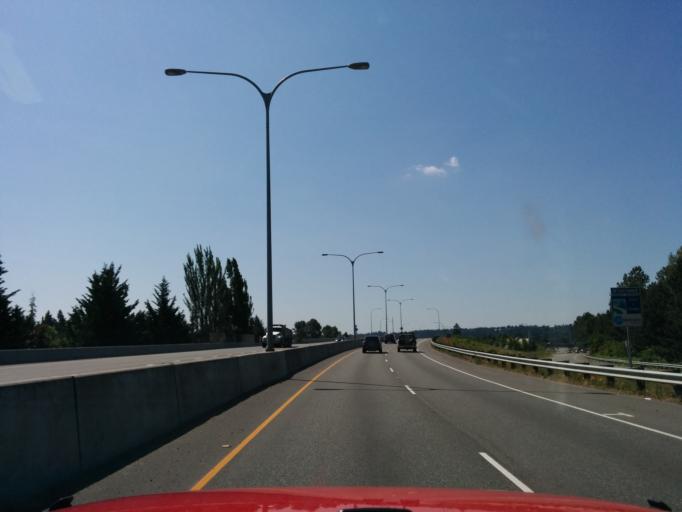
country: US
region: Washington
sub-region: King County
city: Redmond
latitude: 47.6733
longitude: -122.1060
